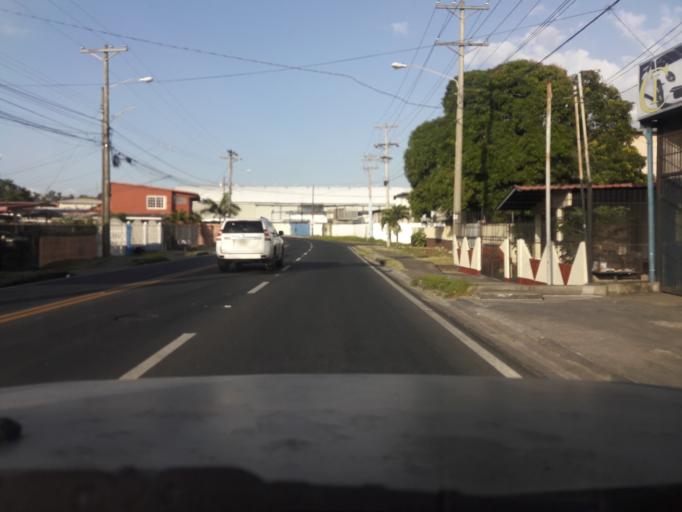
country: PA
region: Panama
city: Panama
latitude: 9.0225
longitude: -79.4977
